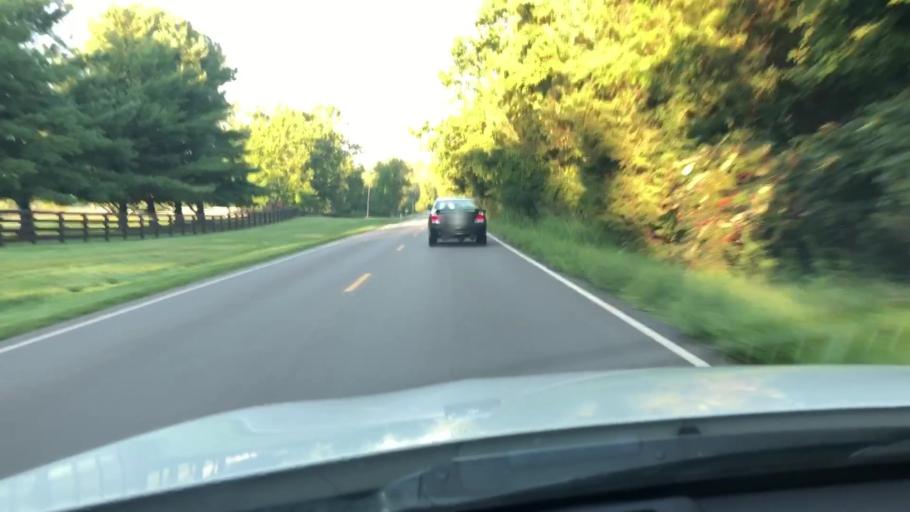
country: US
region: Kentucky
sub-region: Jefferson County
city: Middletown
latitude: 38.2204
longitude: -85.5144
